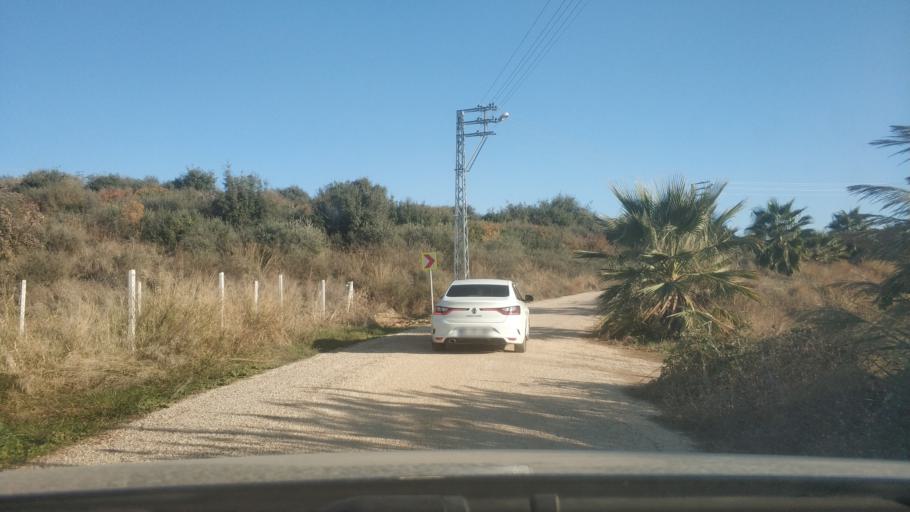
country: TR
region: Adana
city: Adana
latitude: 37.0921
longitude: 35.3050
